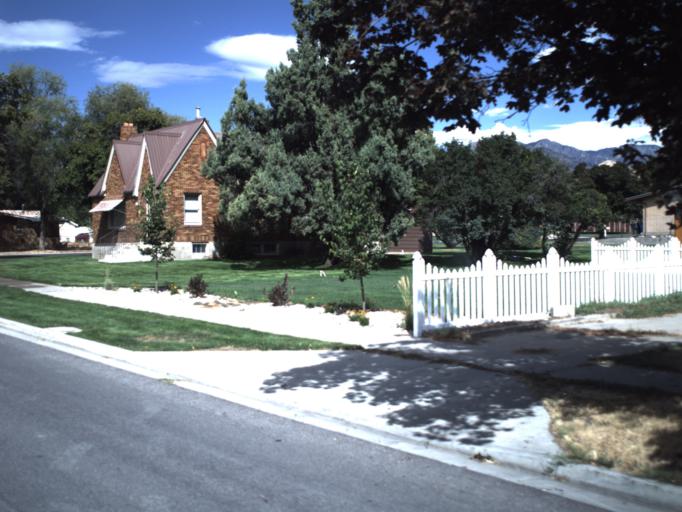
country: US
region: Utah
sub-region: Cache County
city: Smithfield
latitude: 41.8317
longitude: -111.8327
